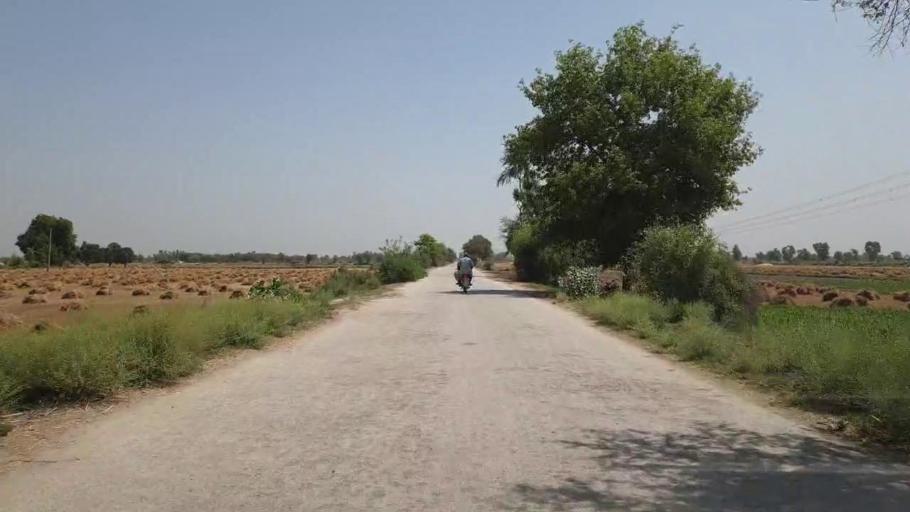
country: PK
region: Sindh
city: Adilpur
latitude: 27.8351
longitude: 69.2597
